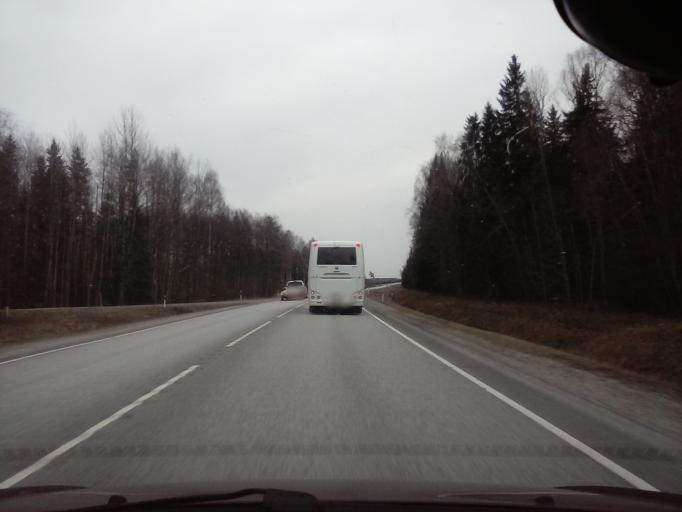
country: EE
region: Jaervamaa
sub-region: Paide linn
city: Paide
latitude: 59.0760
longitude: 25.4239
